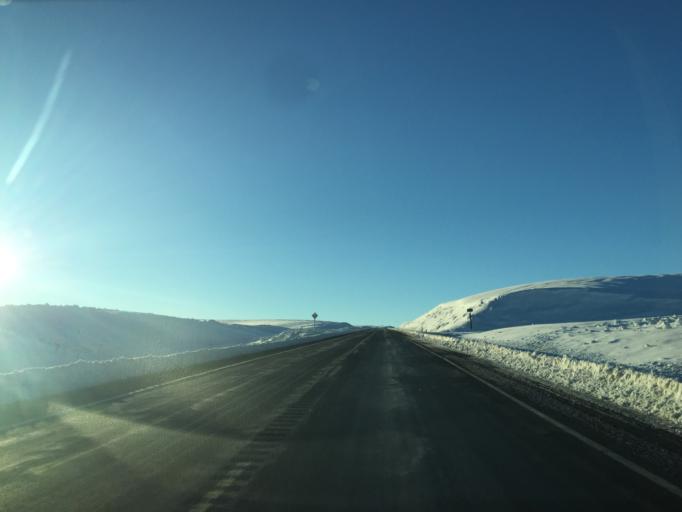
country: US
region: Washington
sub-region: Grant County
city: Soap Lake
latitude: 47.6210
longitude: -119.4043
